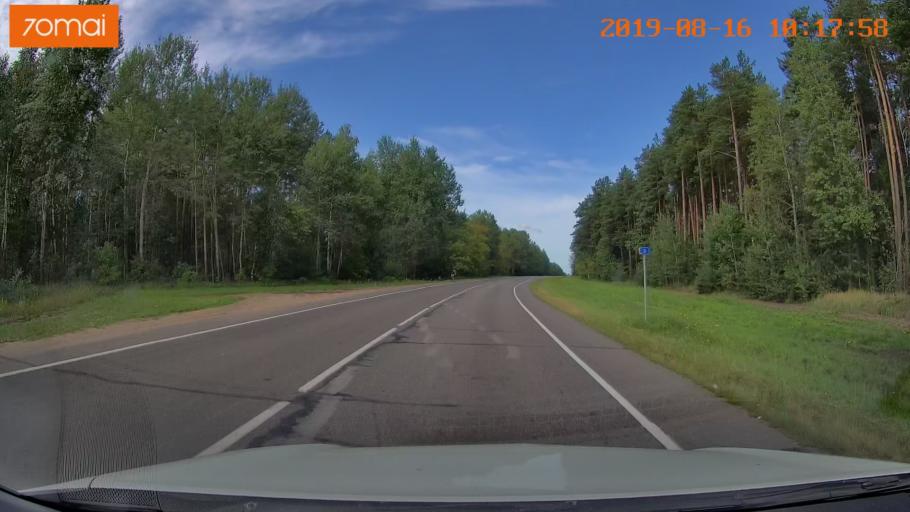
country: BY
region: Mogilev
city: Asipovichy
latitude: 53.3057
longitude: 28.7021
